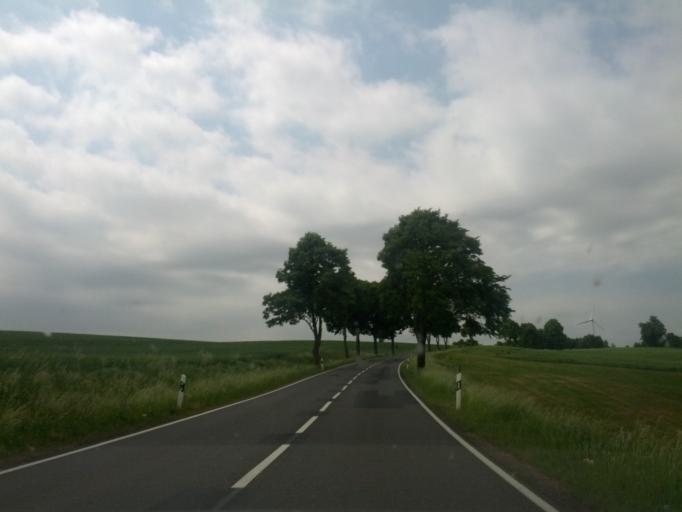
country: DE
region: Thuringia
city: Wolfsburg-Unkeroda
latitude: 50.9331
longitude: 10.2336
